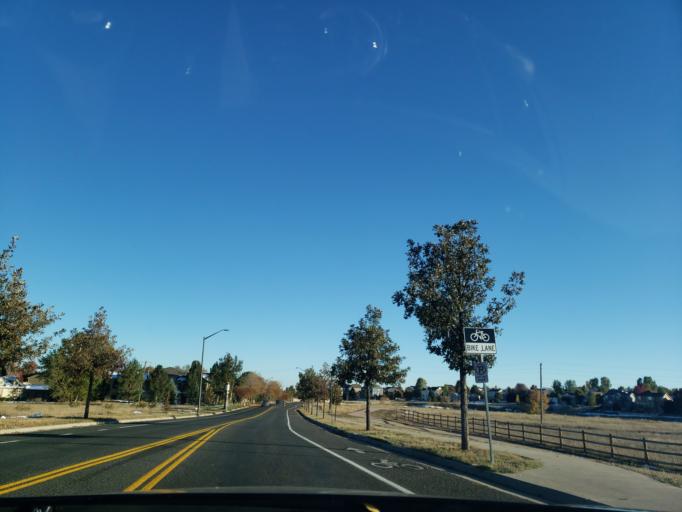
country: US
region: Colorado
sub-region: Larimer County
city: Fort Collins
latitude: 40.5098
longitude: -105.0690
